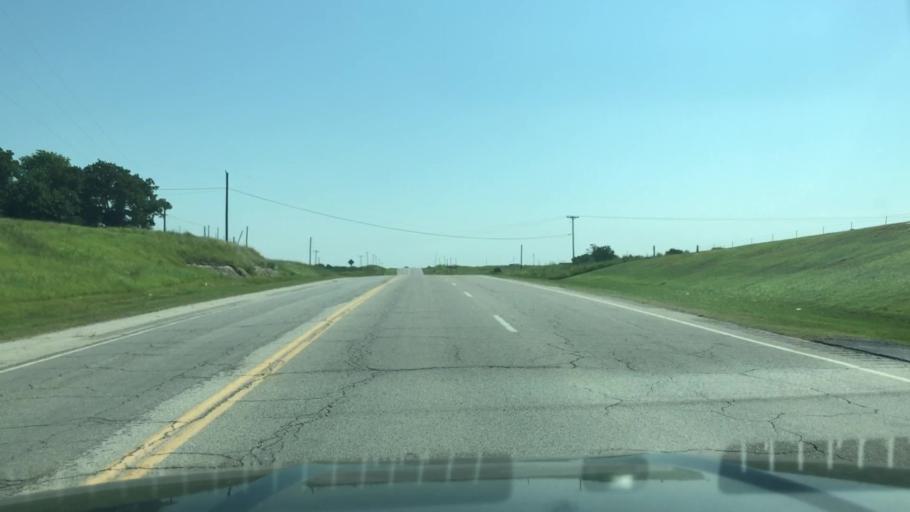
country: US
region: Oklahoma
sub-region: Creek County
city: Drumright
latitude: 35.9910
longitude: -96.5402
